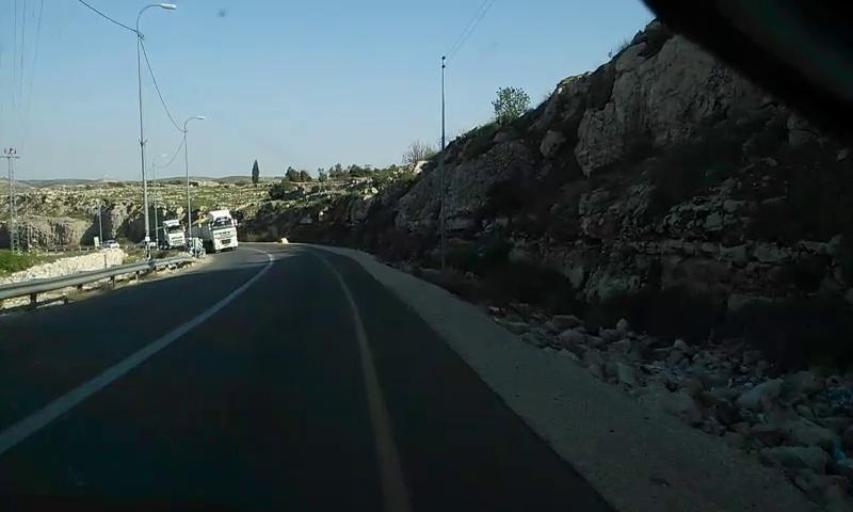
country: PS
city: Khallat ad Dar
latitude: 31.5013
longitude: 35.1122
